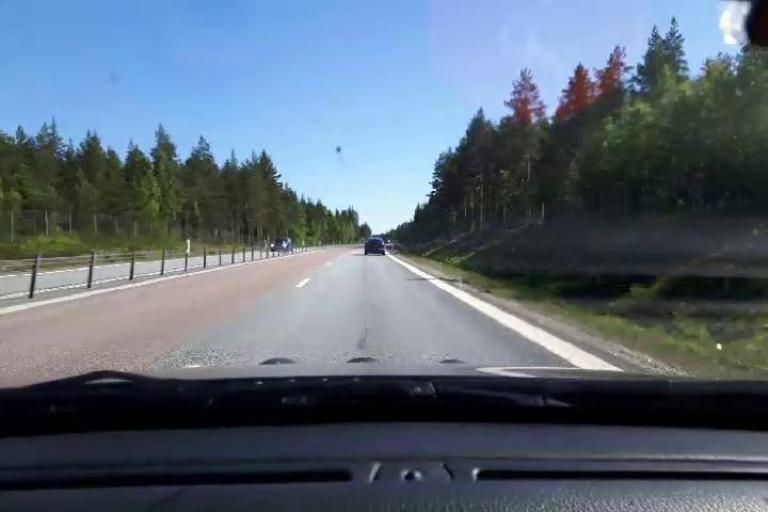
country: SE
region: Gaevleborg
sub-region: Gavle Kommun
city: Norrsundet
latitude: 60.8822
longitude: 17.0449
